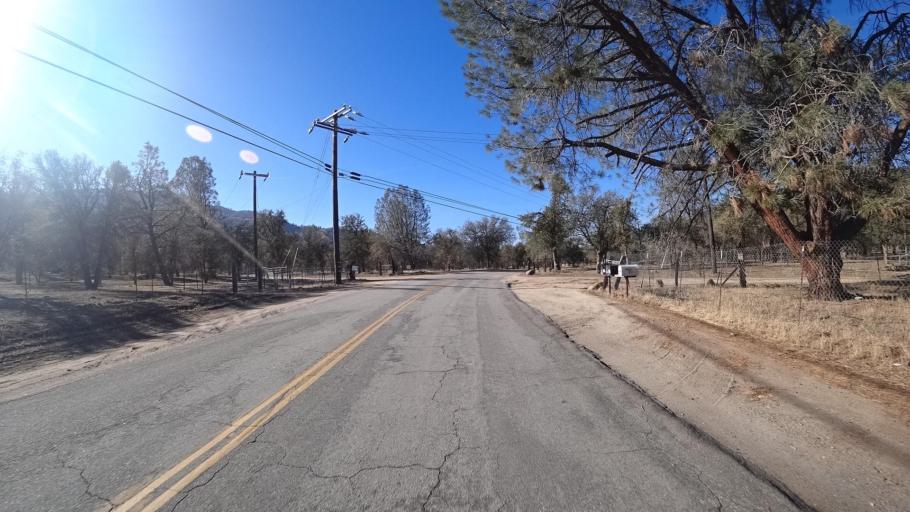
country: US
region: California
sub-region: Kern County
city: Bodfish
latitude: 35.4023
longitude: -118.5095
